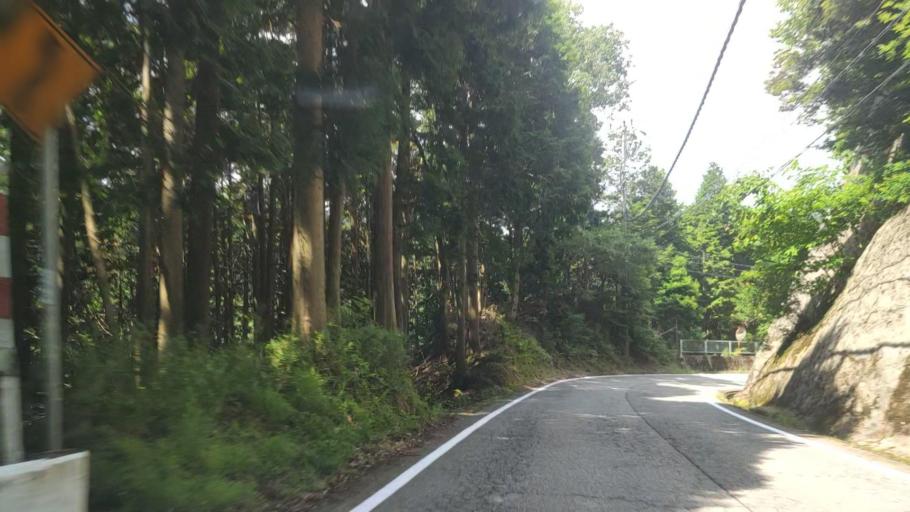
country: JP
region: Hyogo
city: Toyooka
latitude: 35.6417
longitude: 134.7654
